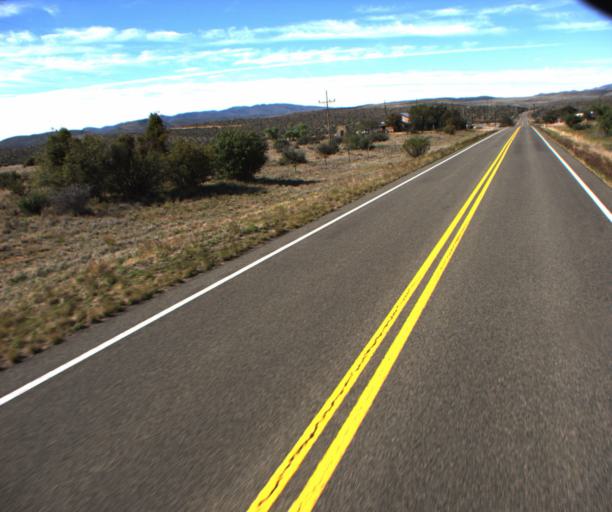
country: US
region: Arizona
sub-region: Yavapai County
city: Prescott
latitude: 34.3721
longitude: -112.6638
